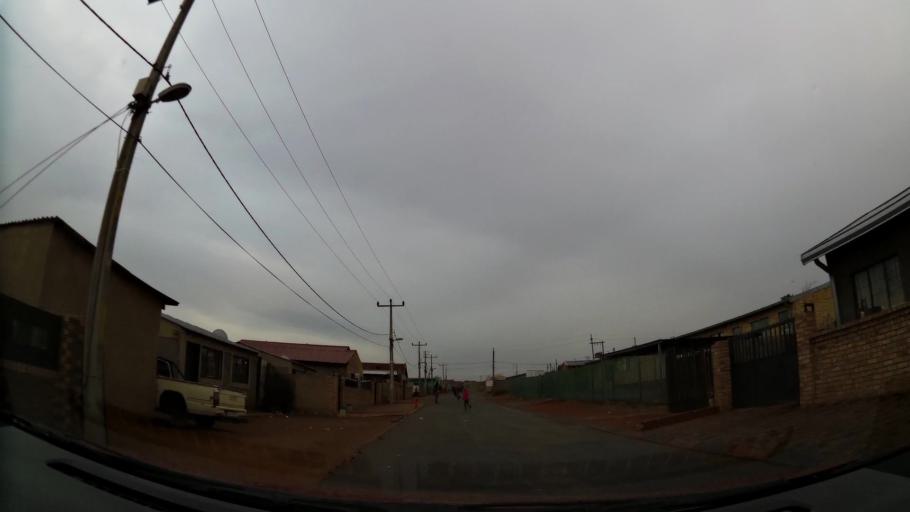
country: ZA
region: Gauteng
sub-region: City of Johannesburg Metropolitan Municipality
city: Roodepoort
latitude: -26.1730
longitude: 27.7880
